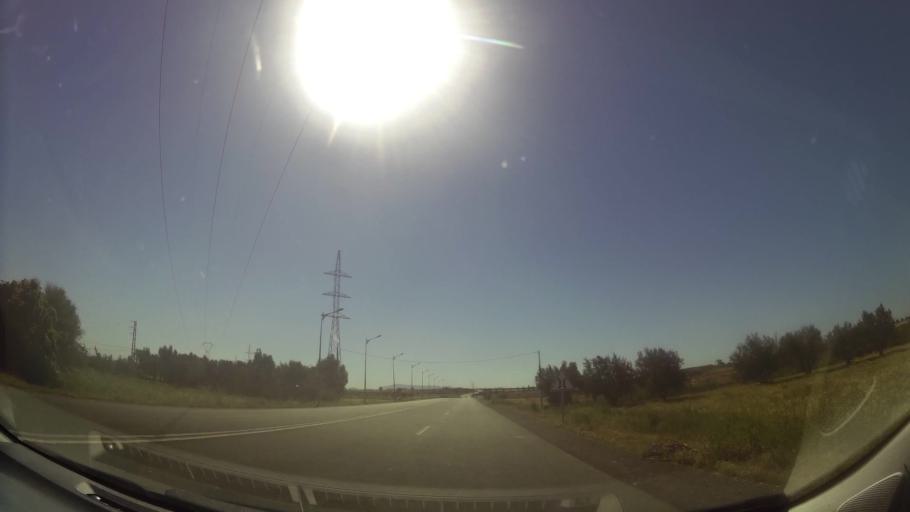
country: MA
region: Oriental
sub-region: Oujda-Angad
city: Oujda
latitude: 34.7397
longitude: -1.8902
